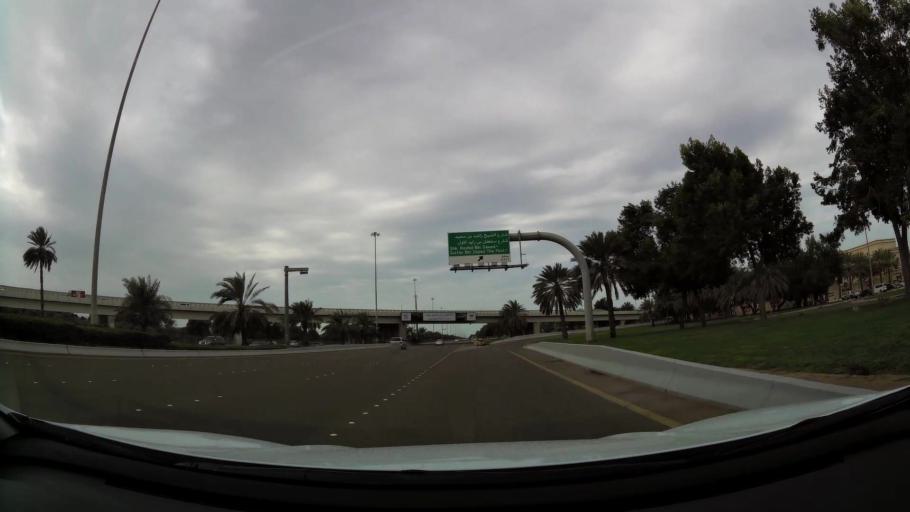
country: AE
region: Abu Dhabi
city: Abu Dhabi
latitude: 24.4225
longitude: 54.4183
